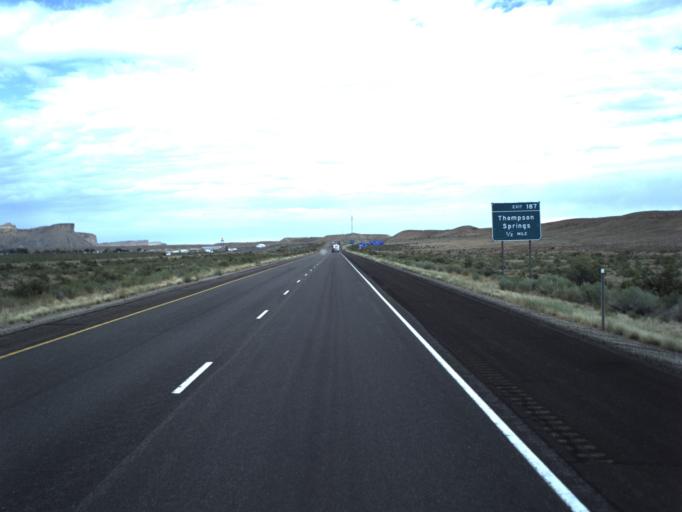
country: US
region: Utah
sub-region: Grand County
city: Moab
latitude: 38.9577
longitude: -109.7401
